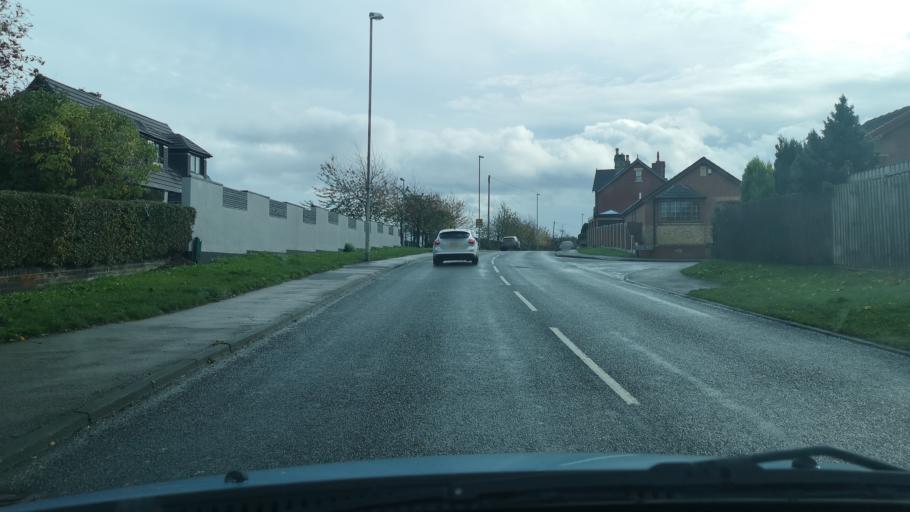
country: GB
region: England
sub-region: City and Borough of Wakefield
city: Hemsworth
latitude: 53.6181
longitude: -1.3563
